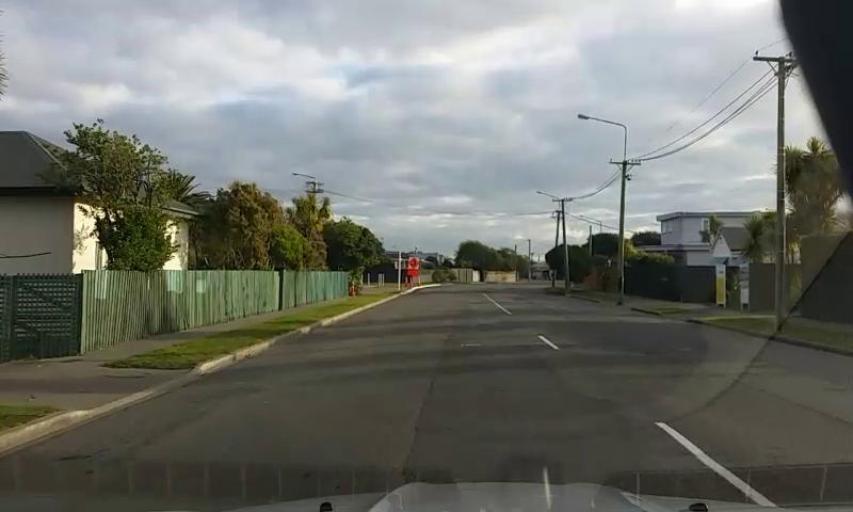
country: NZ
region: Canterbury
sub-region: Christchurch City
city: Christchurch
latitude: -43.5199
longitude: 172.7312
